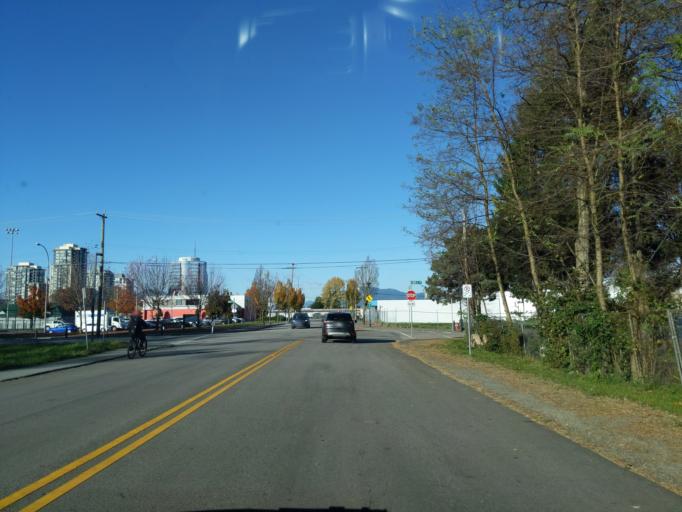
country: CA
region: British Columbia
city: New Westminster
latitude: 49.1941
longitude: -122.8481
